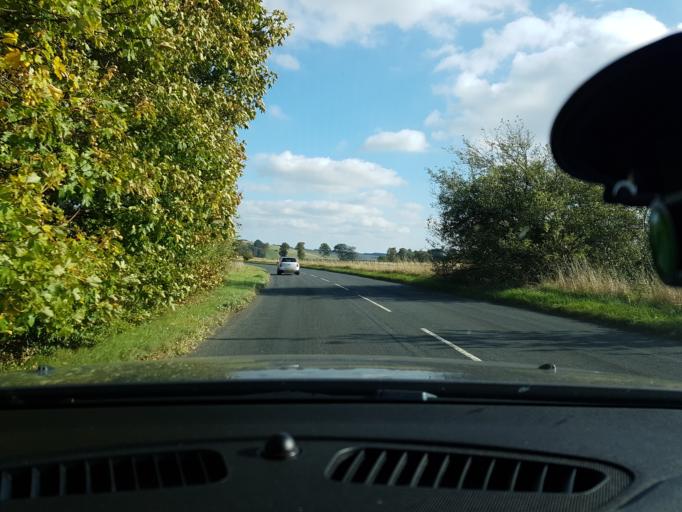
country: GB
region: England
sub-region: Borough of Swindon
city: Bishopstone
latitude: 51.5151
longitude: -1.6472
